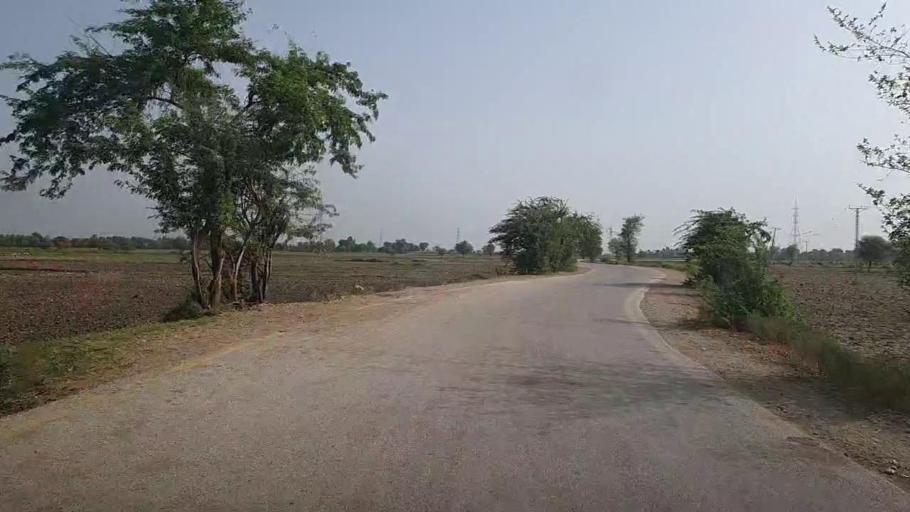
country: PK
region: Sindh
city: Khairpur Nathan Shah
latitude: 27.1045
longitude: 67.7571
